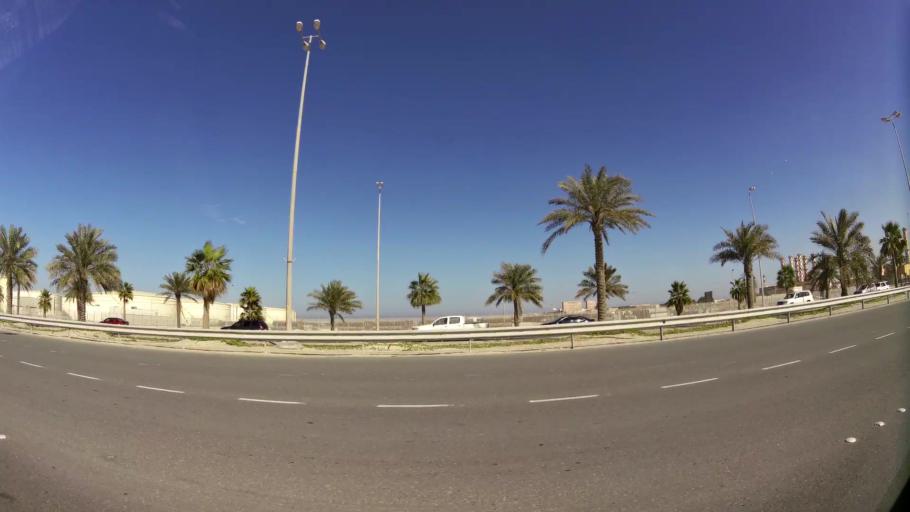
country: BH
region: Muharraq
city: Al Hadd
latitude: 26.2269
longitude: 50.6575
